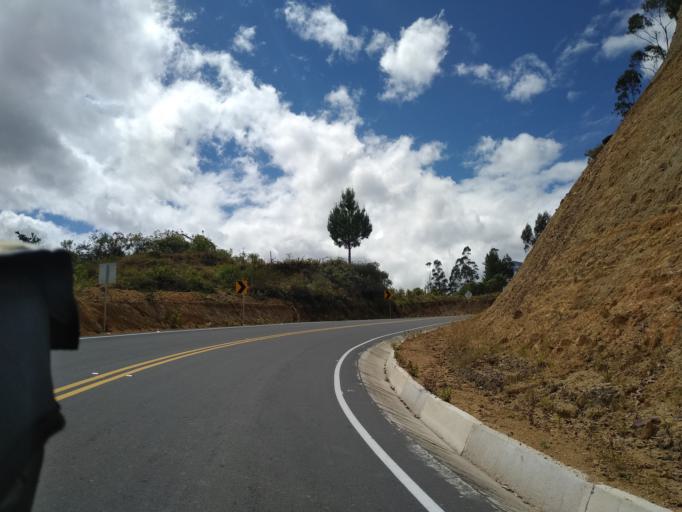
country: EC
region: Cotopaxi
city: Saquisili
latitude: -0.7294
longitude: -78.8984
